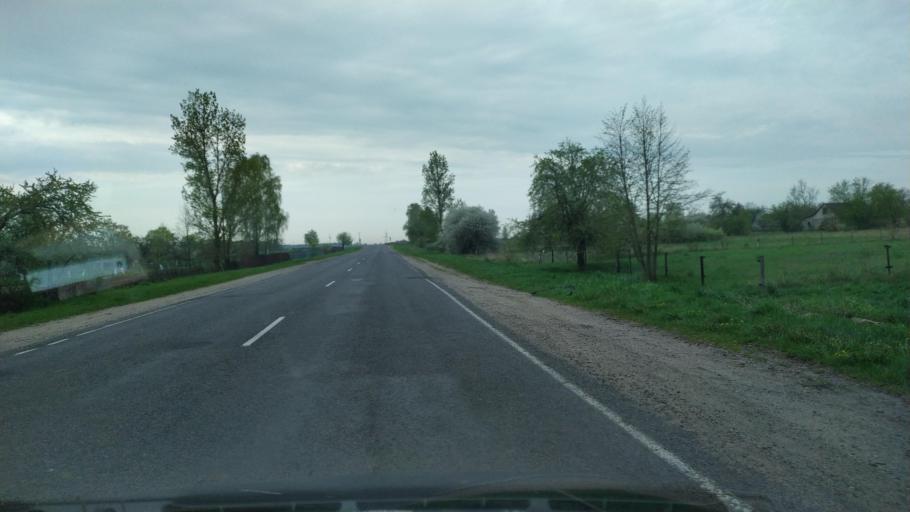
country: BY
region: Brest
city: Kamyanyets
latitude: 52.3137
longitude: 23.9208
